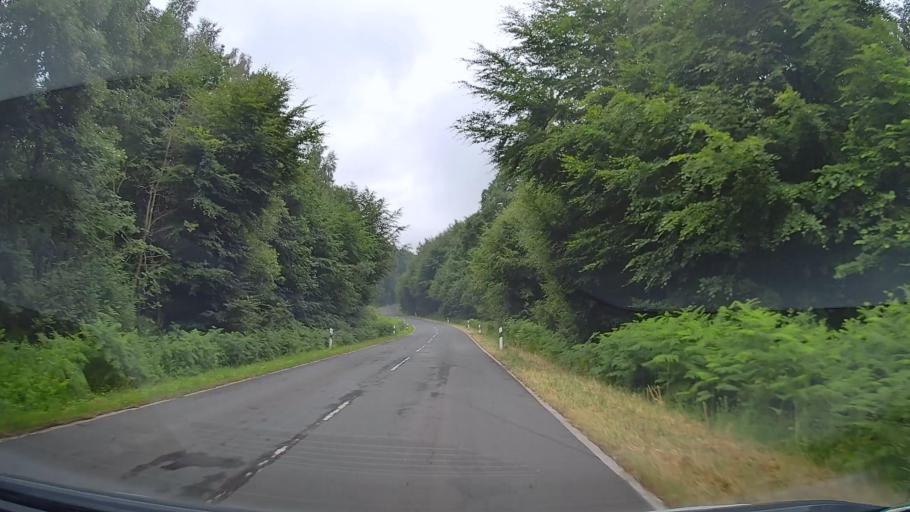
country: DE
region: Lower Saxony
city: Rinteln
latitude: 52.1499
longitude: 9.0531
